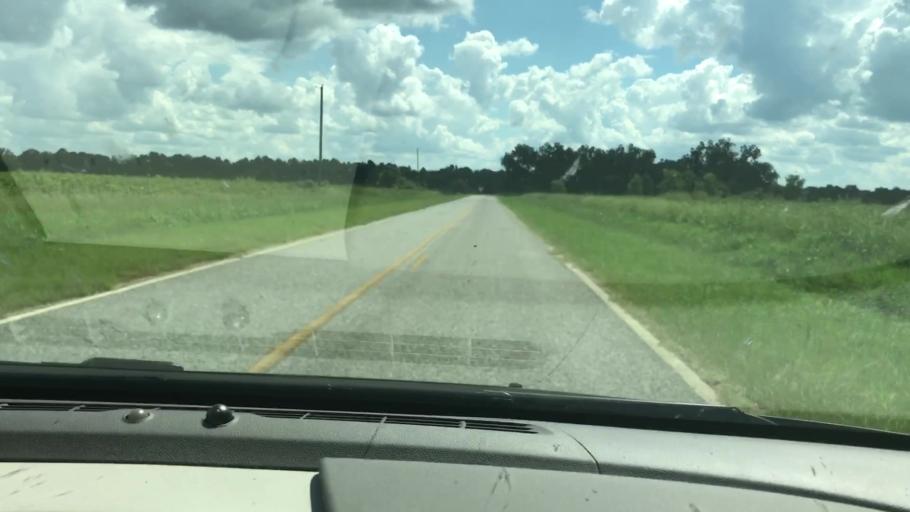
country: US
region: Georgia
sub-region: Quitman County
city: Georgetown
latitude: 31.7583
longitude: -85.0741
